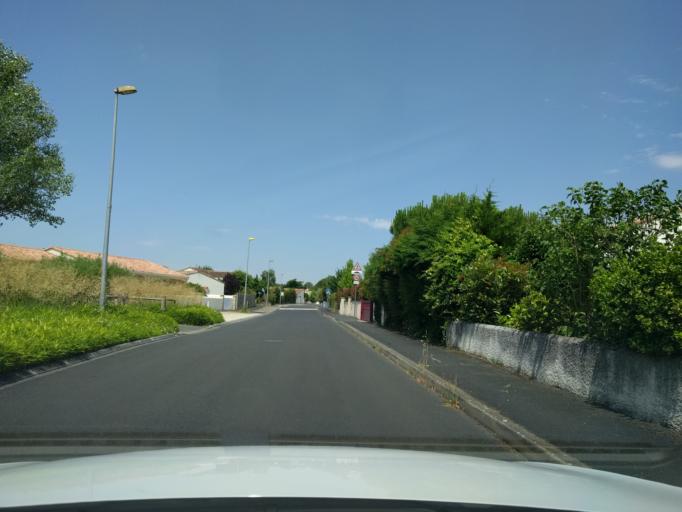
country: FR
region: Poitou-Charentes
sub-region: Departement des Deux-Sevres
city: Niort
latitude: 46.3455
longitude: -0.4801
